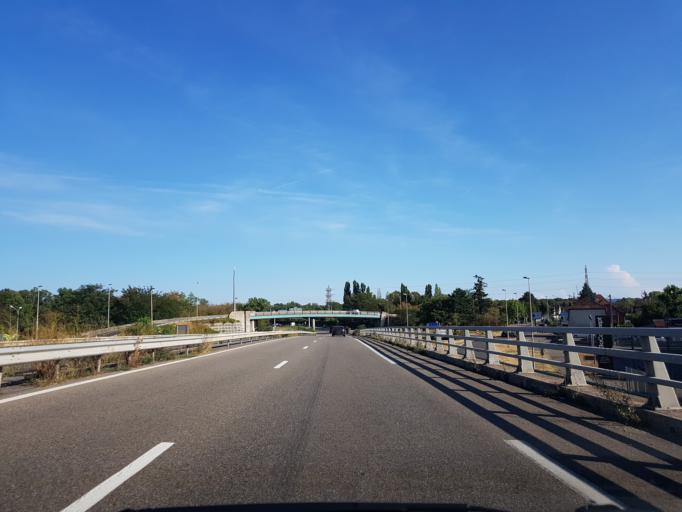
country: FR
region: Alsace
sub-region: Departement du Haut-Rhin
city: Kingersheim
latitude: 47.7890
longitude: 7.3156
